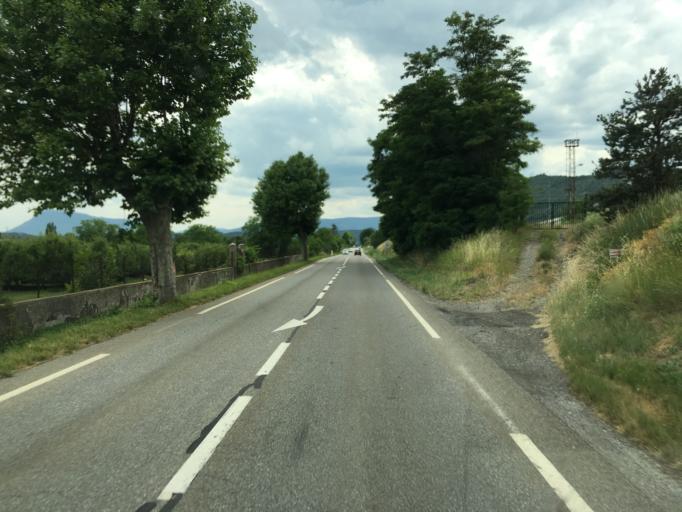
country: FR
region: Provence-Alpes-Cote d'Azur
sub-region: Departement des Hautes-Alpes
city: Veynes
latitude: 44.5296
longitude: 5.8134
